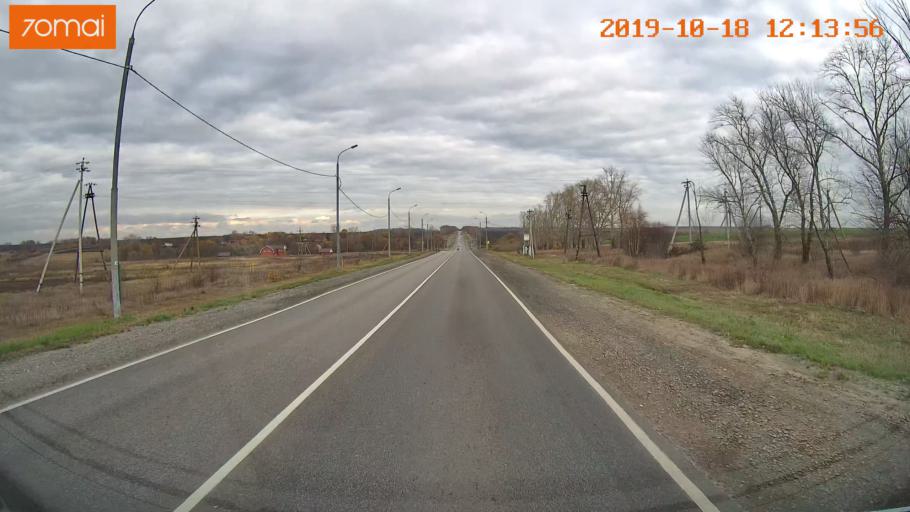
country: RU
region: Rjazan
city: Zakharovo
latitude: 54.4247
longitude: 39.3751
